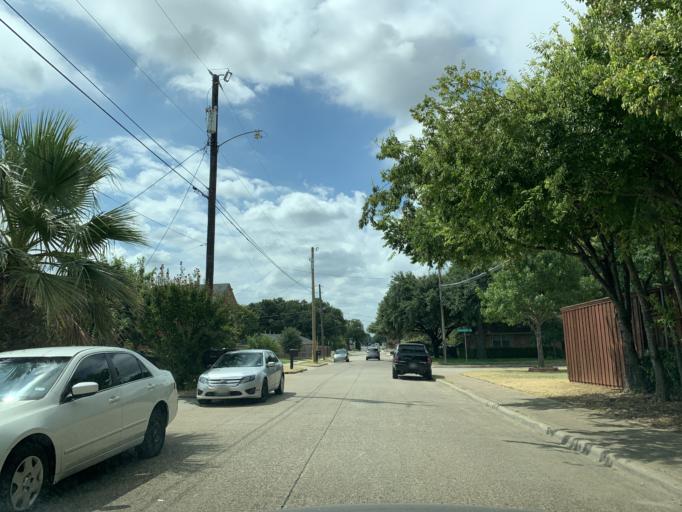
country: US
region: Texas
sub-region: Dallas County
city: Cockrell Hill
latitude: 32.7610
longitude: -96.8688
